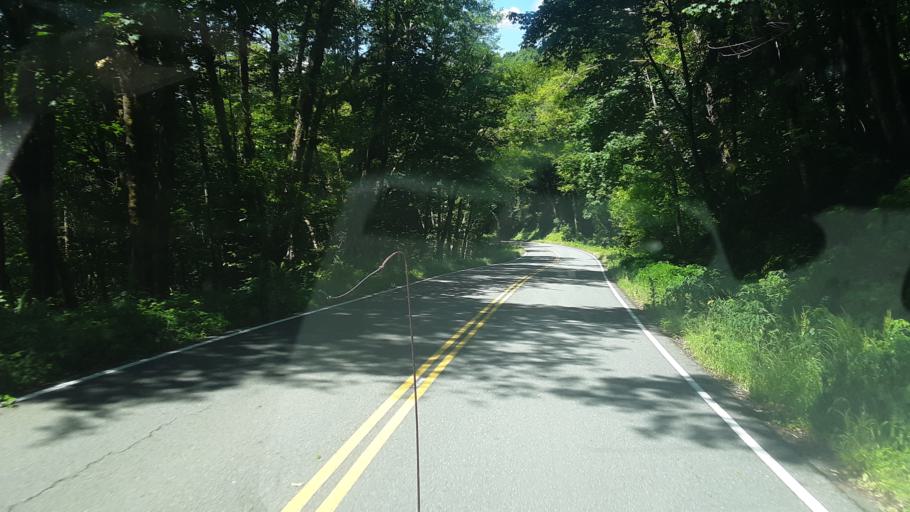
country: US
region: Washington
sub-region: Clark County
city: Yacolt
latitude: 46.0648
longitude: -122.2146
